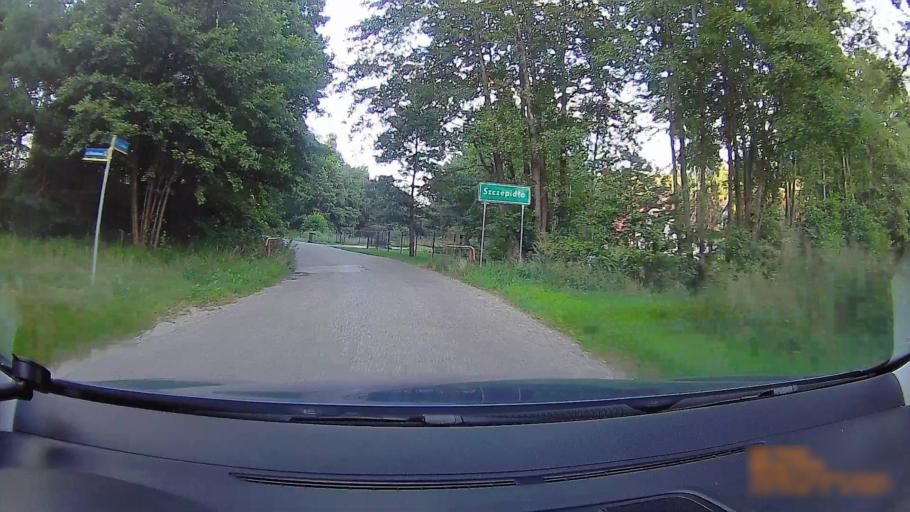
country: PL
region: Greater Poland Voivodeship
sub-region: Konin
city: Konin
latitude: 52.2006
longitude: 18.3176
